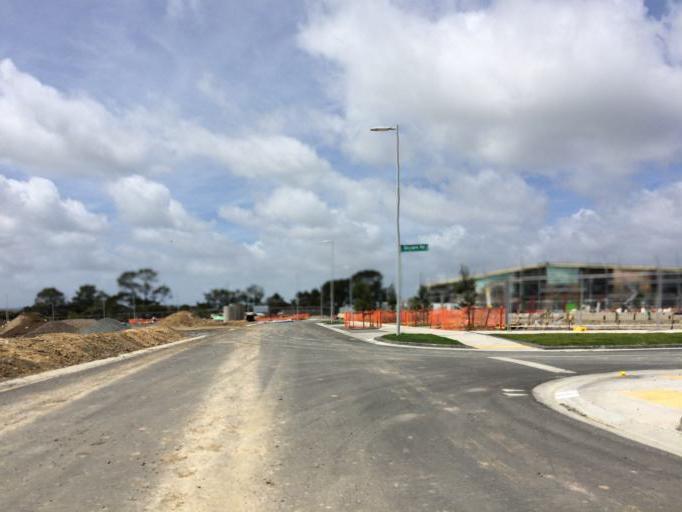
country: NZ
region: Auckland
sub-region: Auckland
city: North Shore
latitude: -36.7936
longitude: 174.6690
